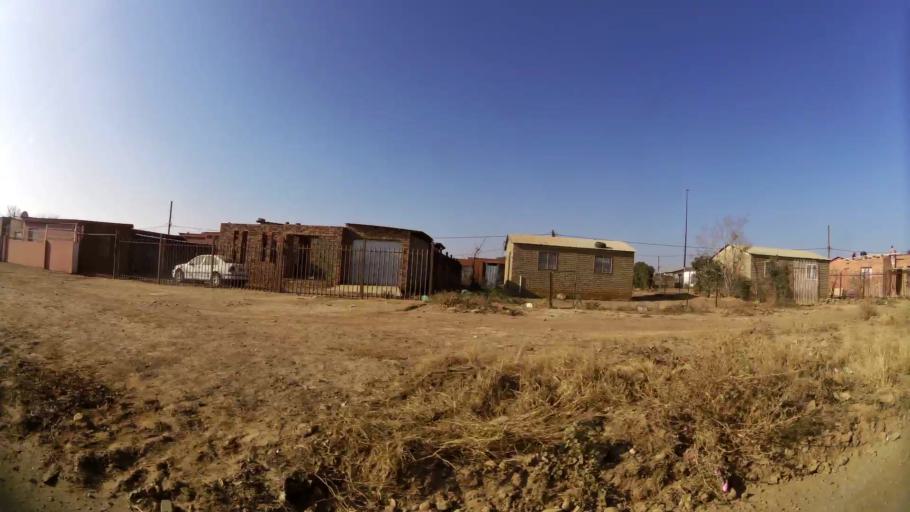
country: ZA
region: Orange Free State
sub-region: Mangaung Metropolitan Municipality
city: Bloemfontein
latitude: -29.2001
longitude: 26.2572
